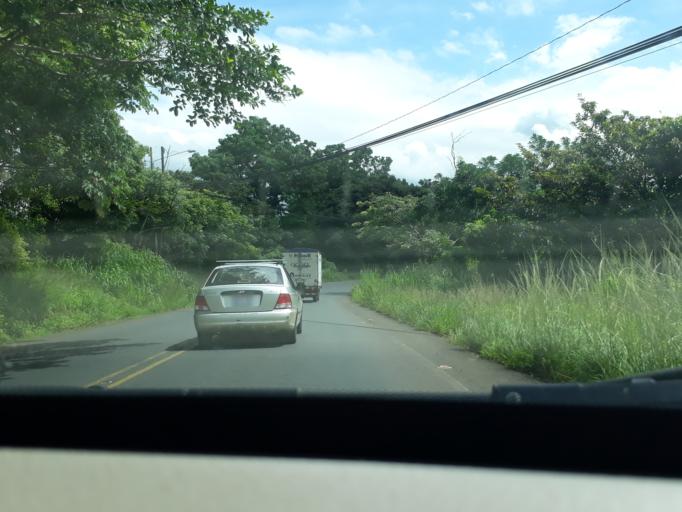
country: CR
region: Alajuela
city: Naranjo
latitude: 10.0430
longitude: -84.3472
